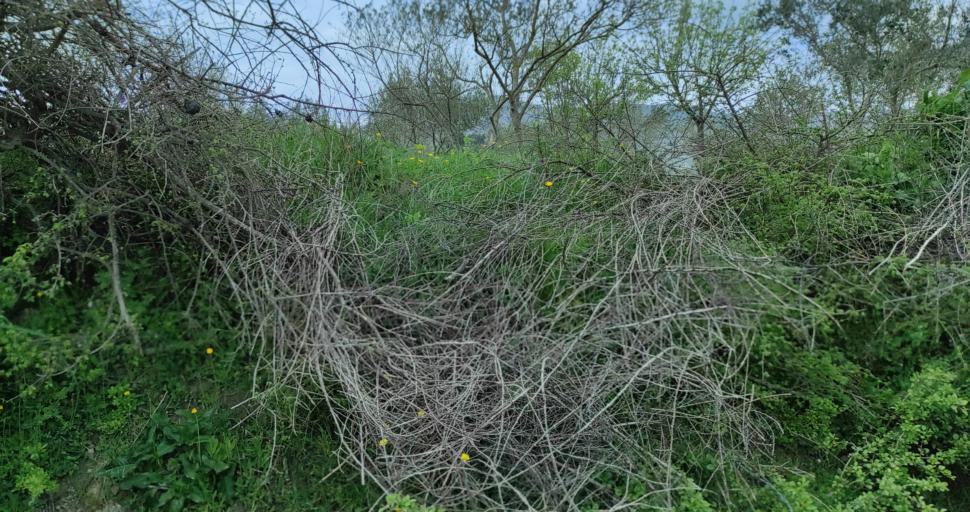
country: AL
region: Shkoder
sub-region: Rrethi i Shkodres
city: Dajc
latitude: 42.0344
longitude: 19.4060
